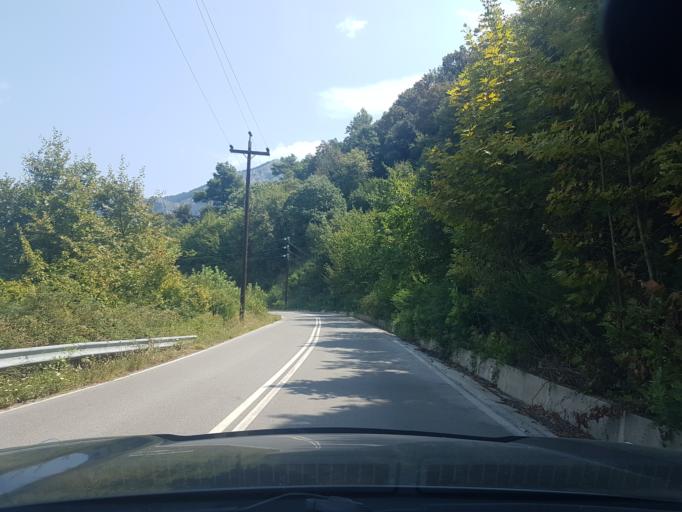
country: GR
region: Central Greece
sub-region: Nomos Evvoias
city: Kymi
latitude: 38.6384
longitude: 23.9413
